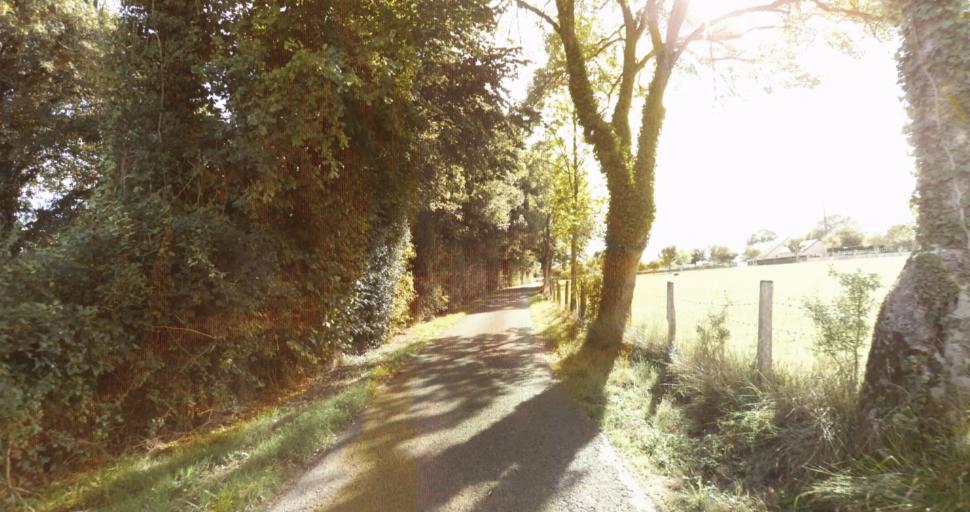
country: FR
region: Lower Normandy
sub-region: Departement de l'Orne
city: Gace
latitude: 48.7125
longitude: 0.2325
